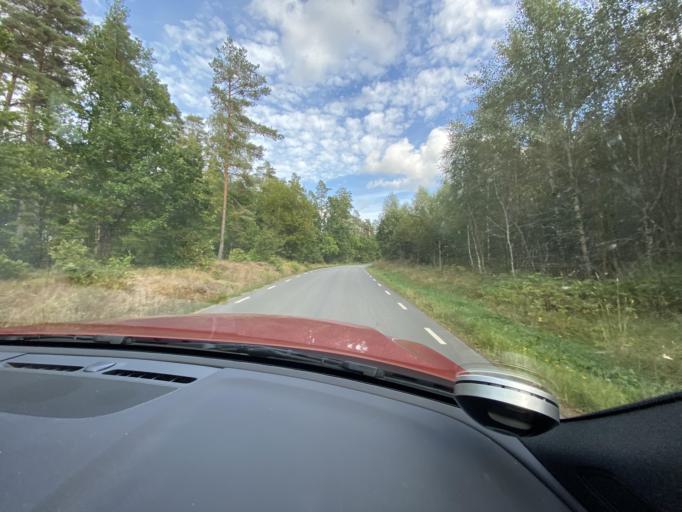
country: SE
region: Skane
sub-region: Hassleholms Kommun
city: Bjarnum
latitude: 56.3580
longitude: 13.8006
